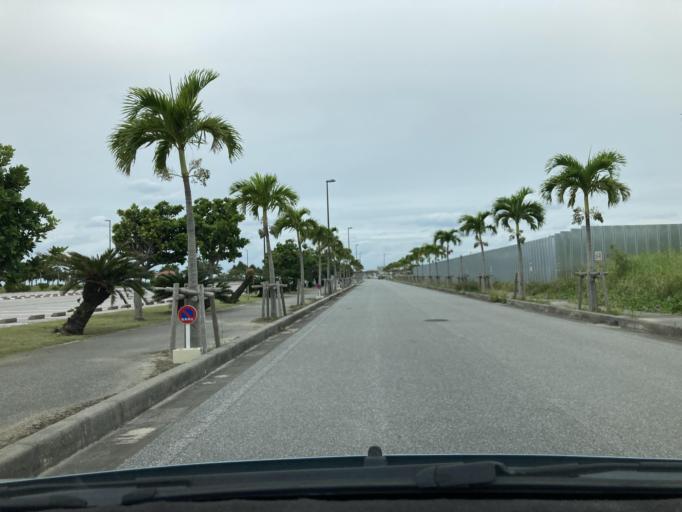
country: JP
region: Okinawa
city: Itoman
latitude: 26.1332
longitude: 127.6520
